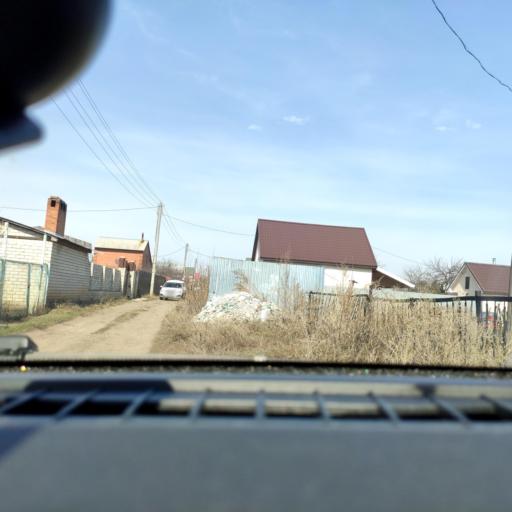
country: RU
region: Samara
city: Podstepki
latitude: 53.5157
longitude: 49.1073
